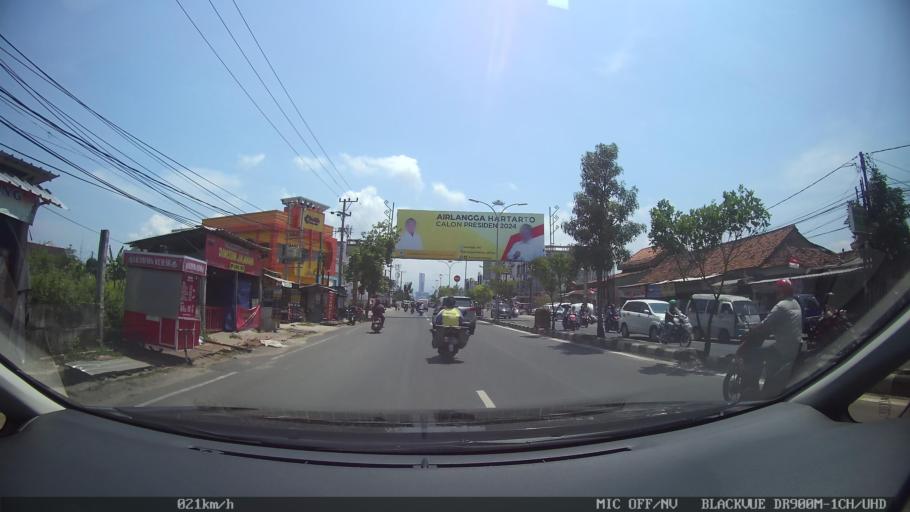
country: ID
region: Lampung
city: Kedaton
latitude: -5.4038
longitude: 105.2802
